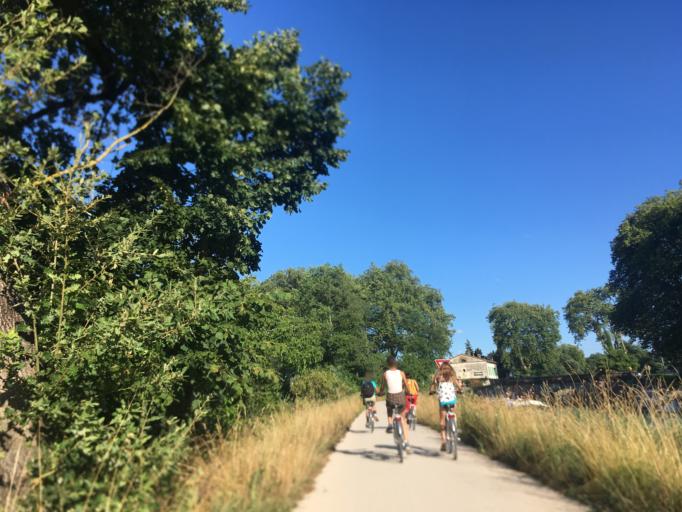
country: FR
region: Midi-Pyrenees
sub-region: Departement de la Haute-Garonne
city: Gardouch
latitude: 43.3926
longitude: 1.6904
